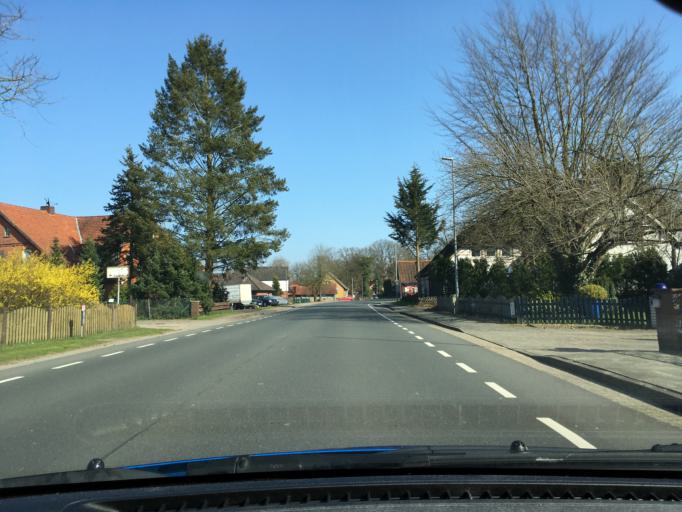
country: DE
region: Lower Saxony
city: Winsen
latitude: 52.6599
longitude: 9.9277
